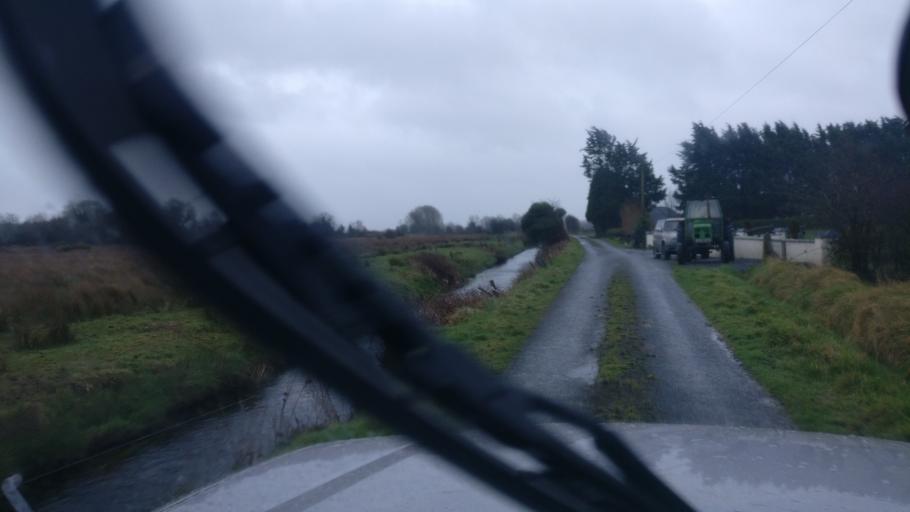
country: IE
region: Connaught
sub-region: County Galway
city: Ballinasloe
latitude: 53.2454
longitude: -8.3446
